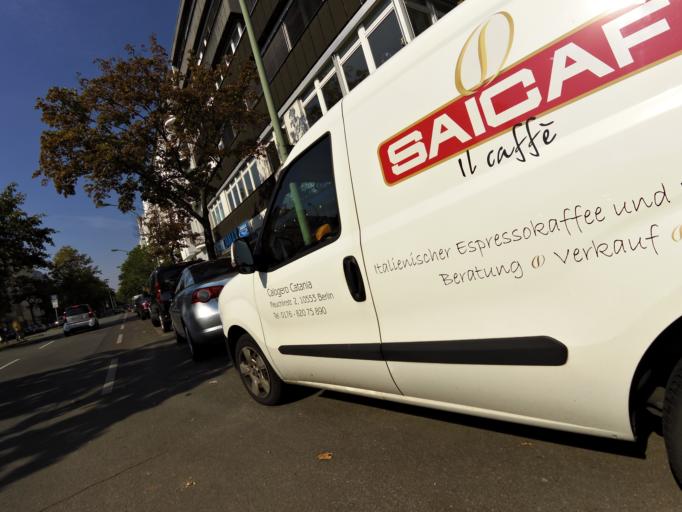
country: DE
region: Berlin
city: Friedenau
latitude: 52.4789
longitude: 13.3312
